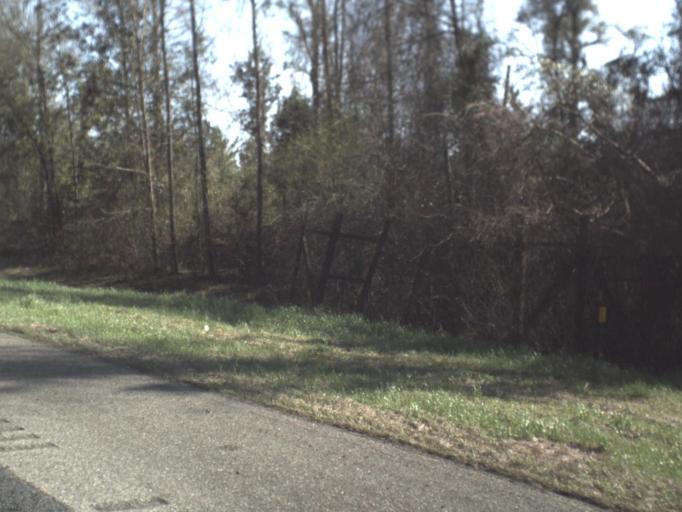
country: US
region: Florida
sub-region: Gadsden County
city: Gretna
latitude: 30.5831
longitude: -84.7117
